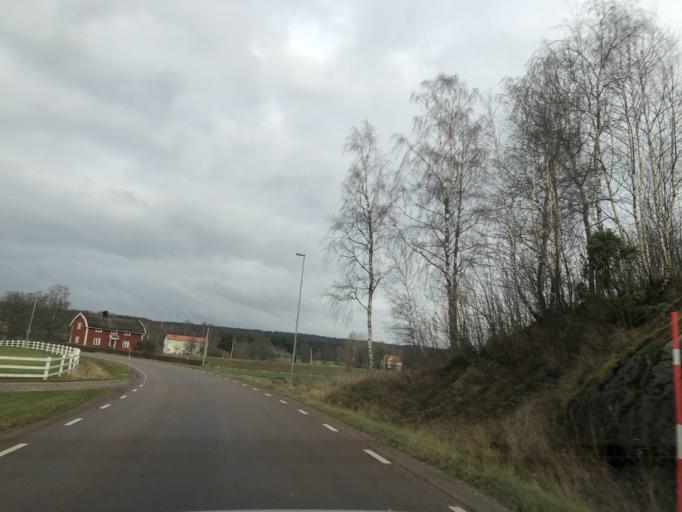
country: SE
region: Vaestra Goetaland
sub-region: Boras Kommun
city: Dalsjofors
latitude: 57.8253
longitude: 13.1582
